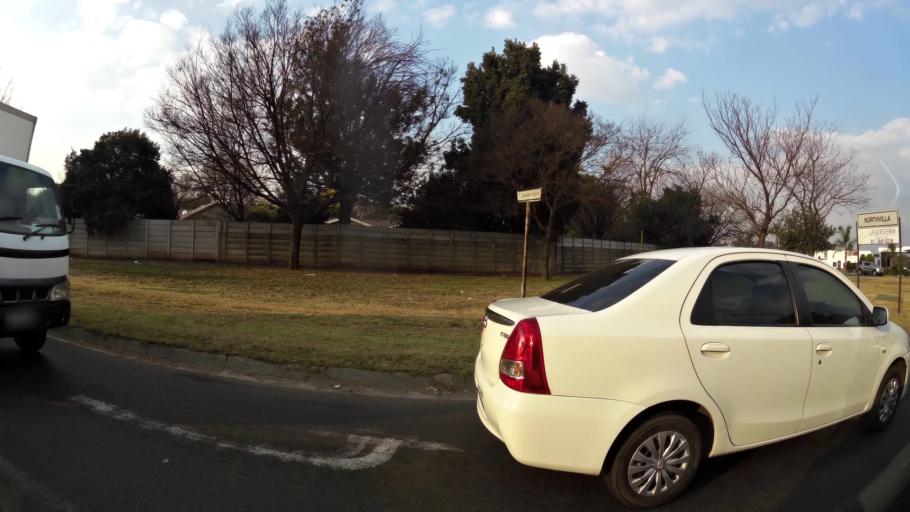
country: ZA
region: Gauteng
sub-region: Ekurhuleni Metropolitan Municipality
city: Benoni
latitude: -26.1386
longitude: 28.2942
